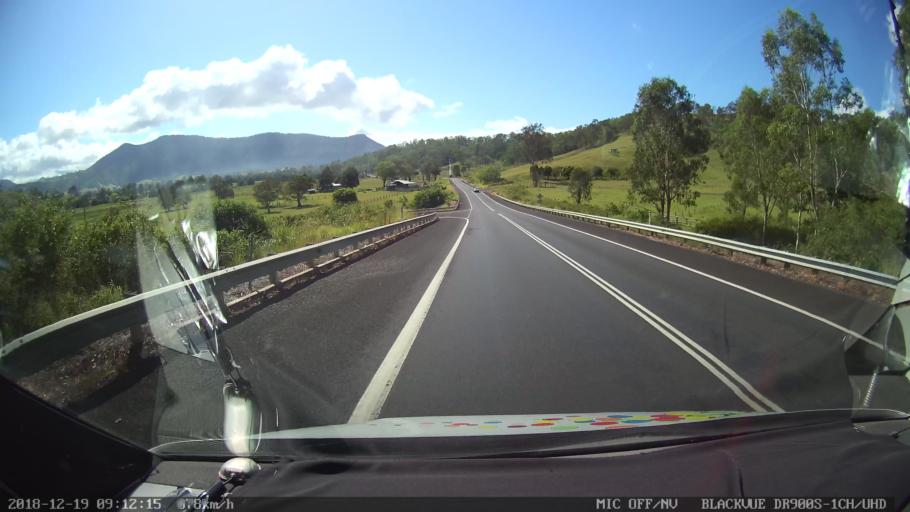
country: AU
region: New South Wales
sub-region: Kyogle
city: Kyogle
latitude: -28.4959
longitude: 152.9478
